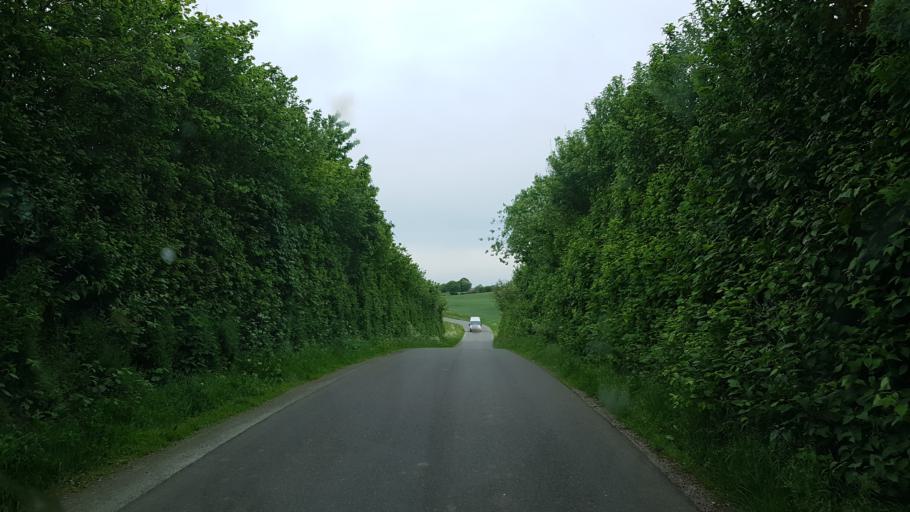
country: DK
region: South Denmark
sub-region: Nordfyns Kommune
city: Bogense
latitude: 55.4739
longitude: 10.0829
